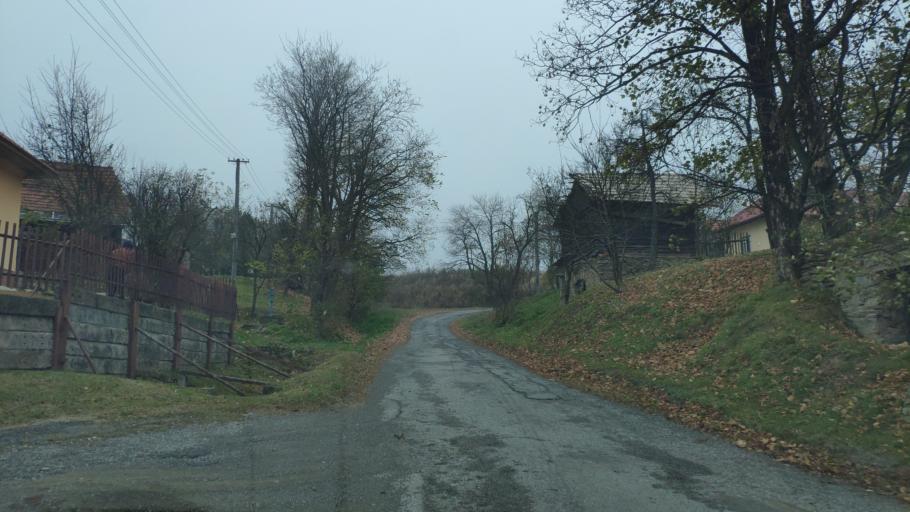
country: SK
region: Presovsky
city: Sabinov
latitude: 49.1474
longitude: 21.2388
